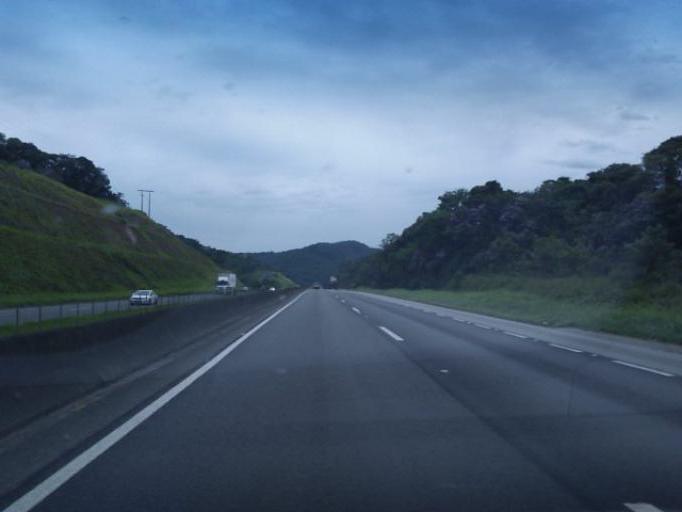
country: BR
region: Sao Paulo
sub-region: Juquia
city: Juquia
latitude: -24.3493
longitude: -47.6526
